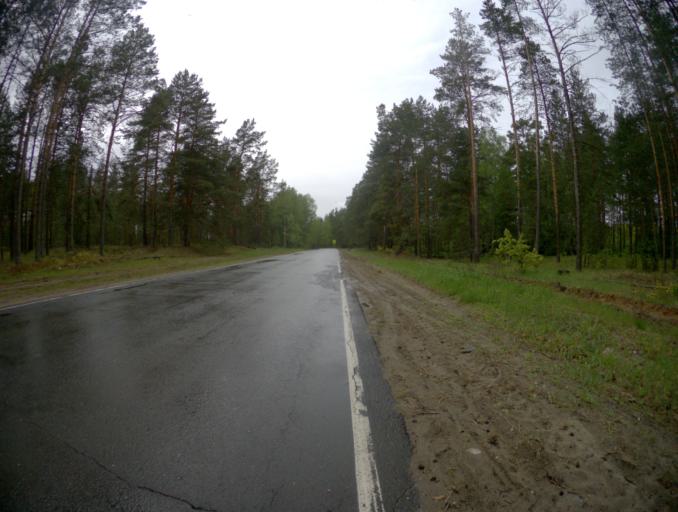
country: RU
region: Vladimir
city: Velikodvorskiy
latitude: 55.3743
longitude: 40.7783
